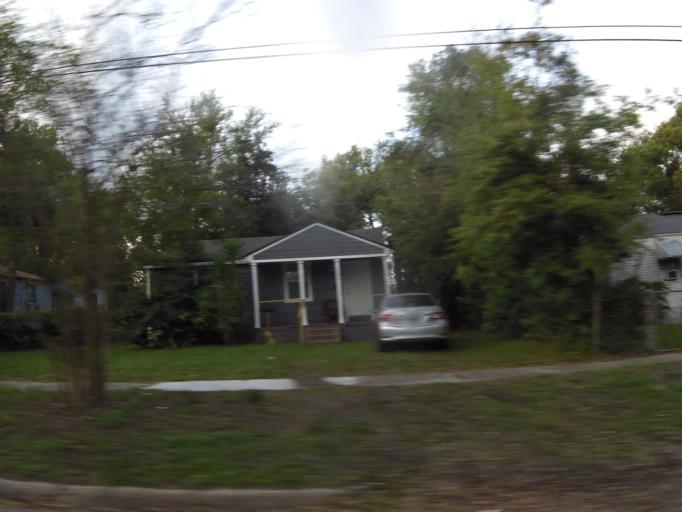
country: US
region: Florida
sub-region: Duval County
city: Jacksonville
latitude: 30.3597
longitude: -81.6316
